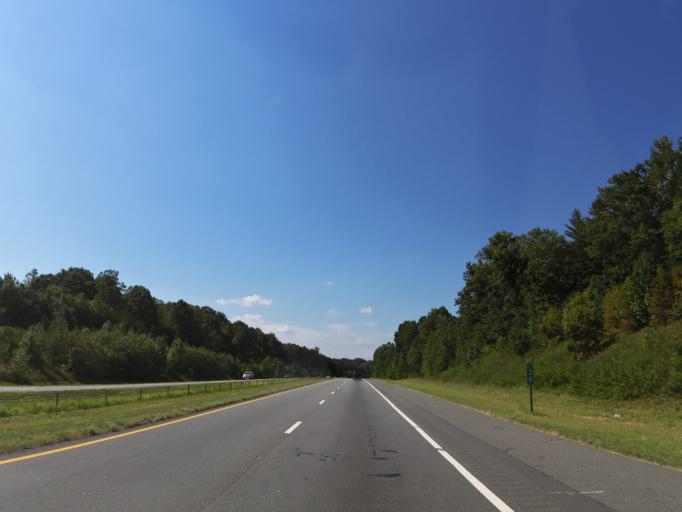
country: US
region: North Carolina
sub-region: Catawba County
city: Mountain View
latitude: 35.6609
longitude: -81.3220
